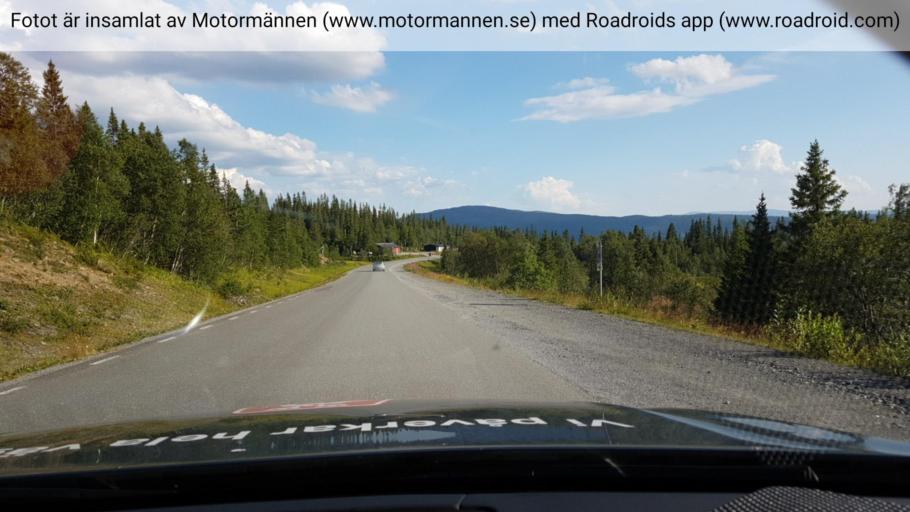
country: SE
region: Jaemtland
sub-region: Are Kommun
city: Are
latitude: 63.4251
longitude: 13.0171
